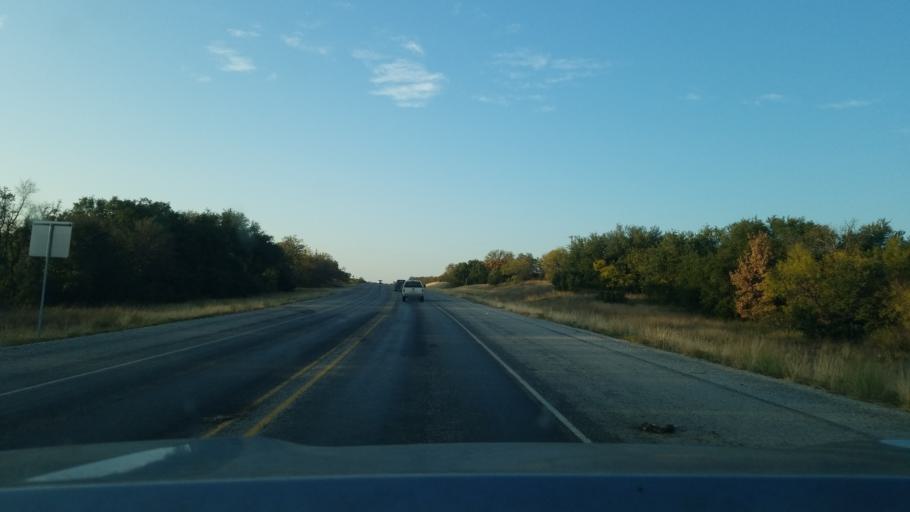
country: US
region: Texas
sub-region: Eastland County
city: Cisco
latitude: 32.3455
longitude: -98.9595
